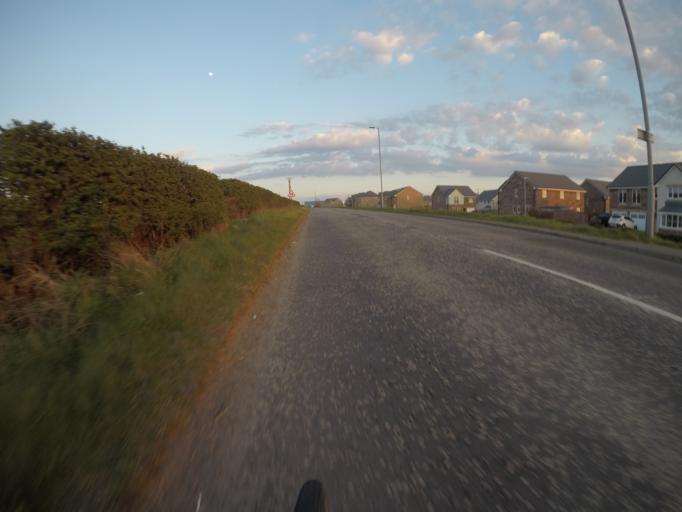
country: GB
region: Scotland
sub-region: South Ayrshire
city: Troon
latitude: 55.5641
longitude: -4.6366
